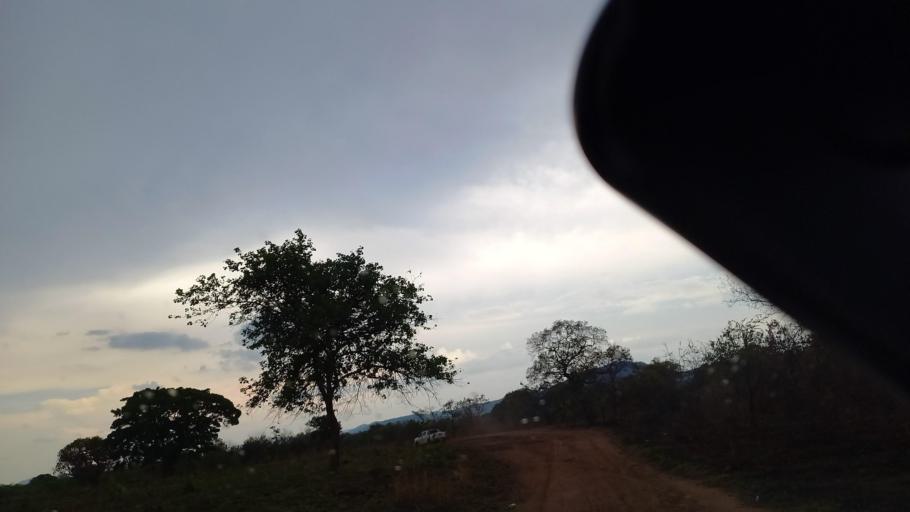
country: ZM
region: Lusaka
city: Kafue
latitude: -15.9930
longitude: 28.2731
